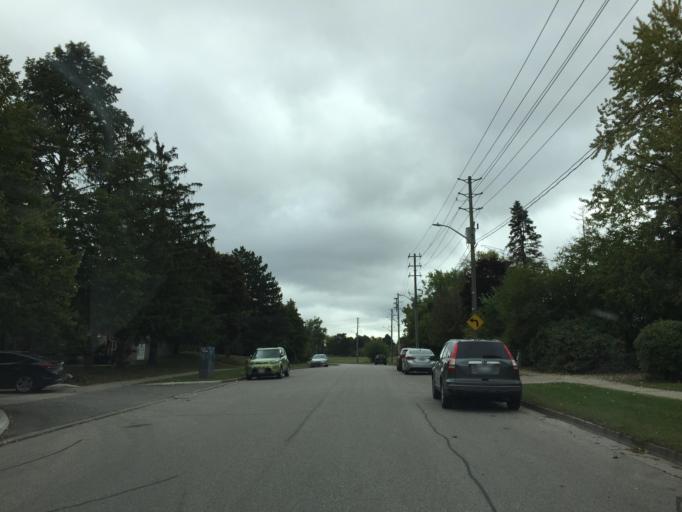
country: CA
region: Ontario
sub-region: Wellington County
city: Guelph
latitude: 43.5172
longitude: -80.2445
